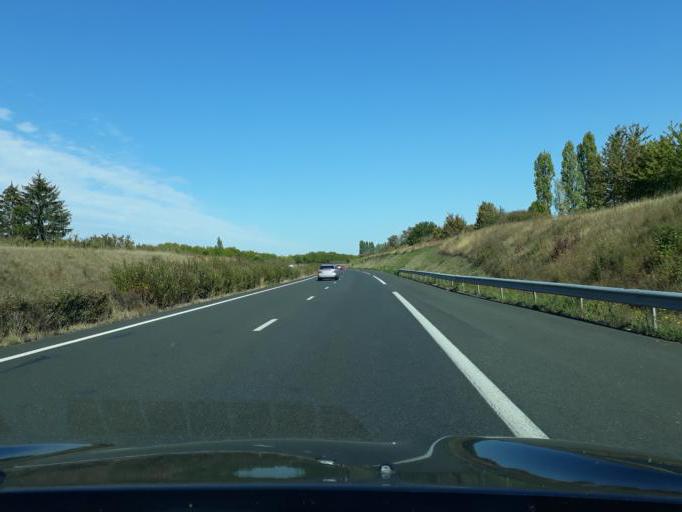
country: FR
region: Centre
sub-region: Departement d'Indre-et-Loire
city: Ballan-Mire
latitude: 47.3243
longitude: 0.6031
